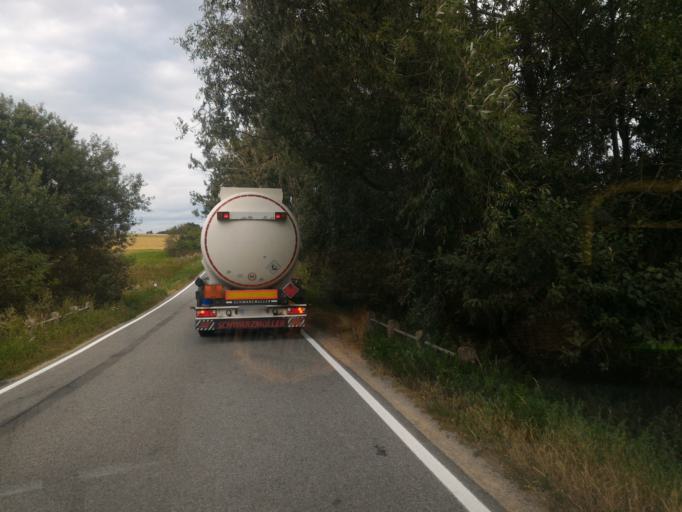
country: CZ
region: Vysocina
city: Zeletava
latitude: 49.1629
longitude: 15.5837
